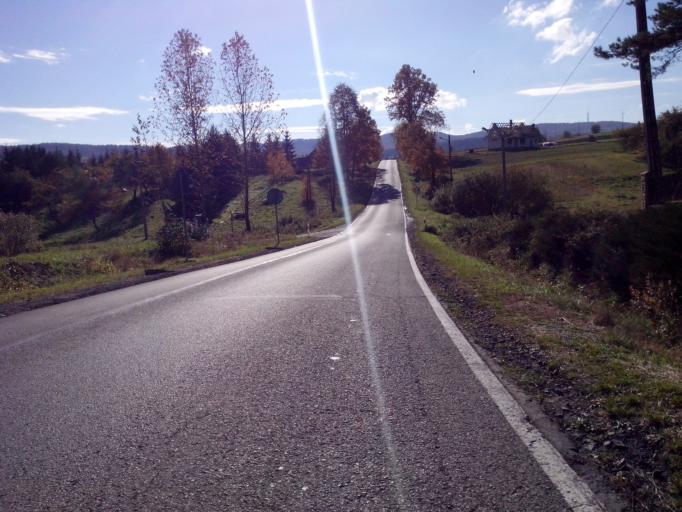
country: PL
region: Subcarpathian Voivodeship
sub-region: Powiat strzyzowski
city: Jawornik
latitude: 49.7914
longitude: 21.8588
